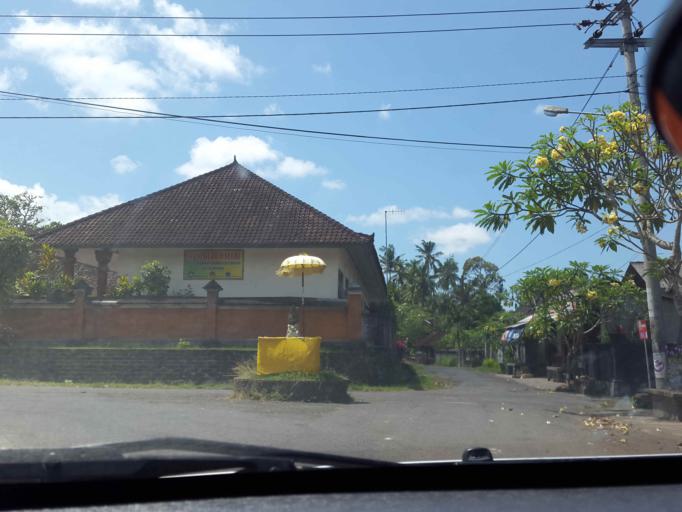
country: ID
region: Bali
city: Banjar Wangsian
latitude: -8.4991
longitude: 115.3981
